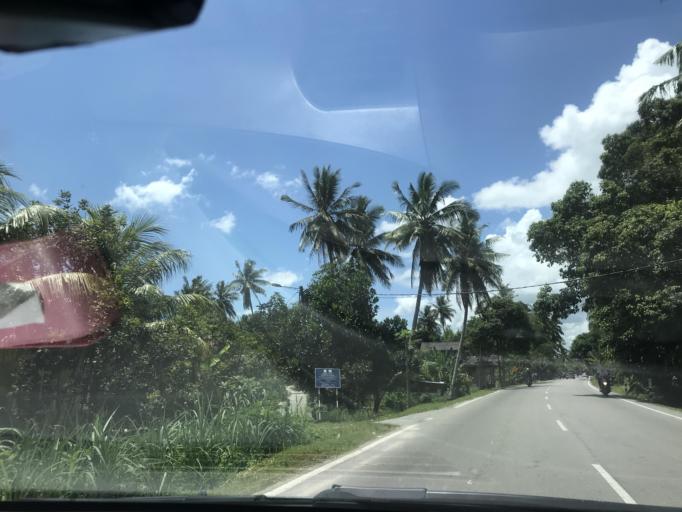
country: MY
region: Kelantan
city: Tumpat
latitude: 6.1946
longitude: 102.1410
